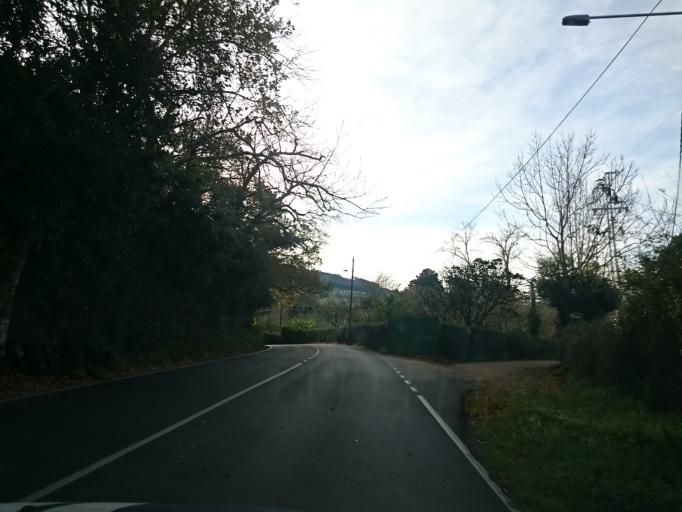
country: ES
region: Asturias
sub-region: Province of Asturias
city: Gijon
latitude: 43.5145
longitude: -5.6226
